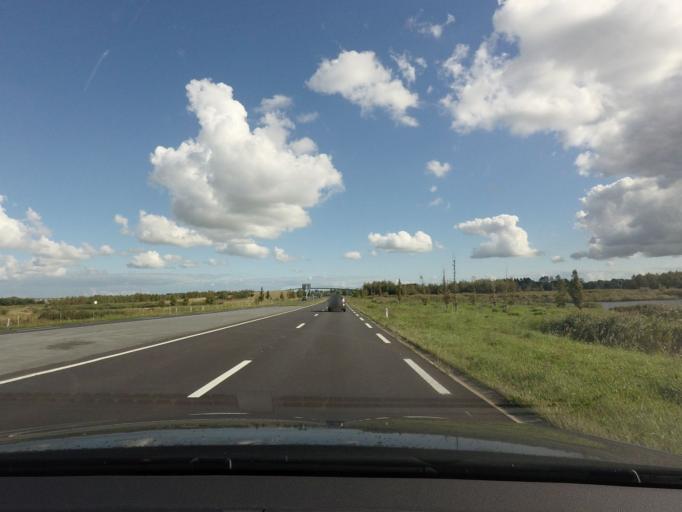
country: NL
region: North Holland
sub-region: Gemeente Langedijk
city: Broek op Langedijk
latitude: 52.6393
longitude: 4.7977
